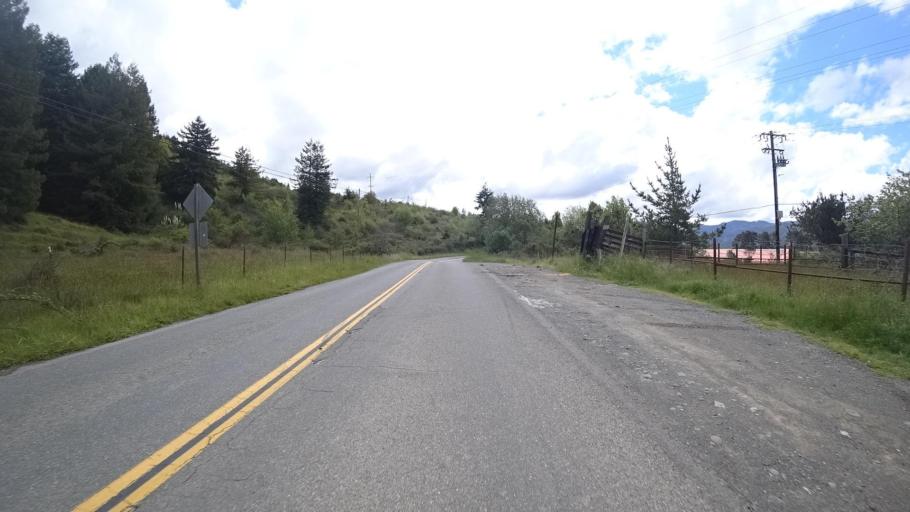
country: US
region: California
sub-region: Humboldt County
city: Blue Lake
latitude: 40.8924
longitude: -124.0009
